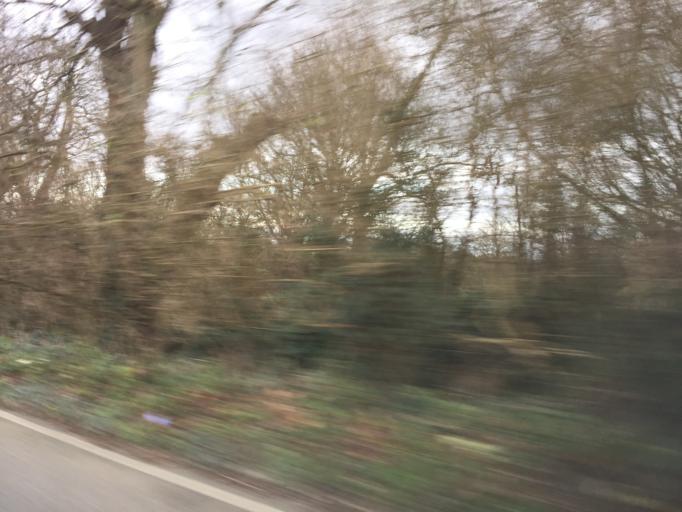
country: GB
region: Wales
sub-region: Monmouthshire
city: Chepstow
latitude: 51.6150
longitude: -2.7130
